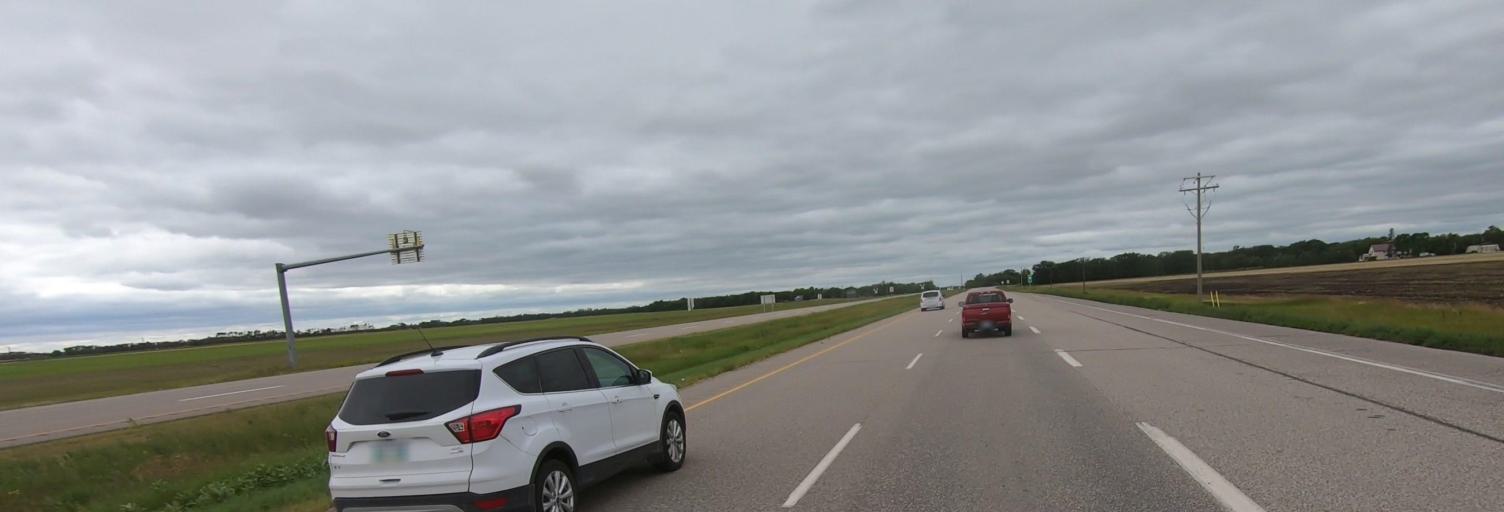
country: CA
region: Manitoba
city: Portage la Prairie
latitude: 49.9752
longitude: -98.4707
